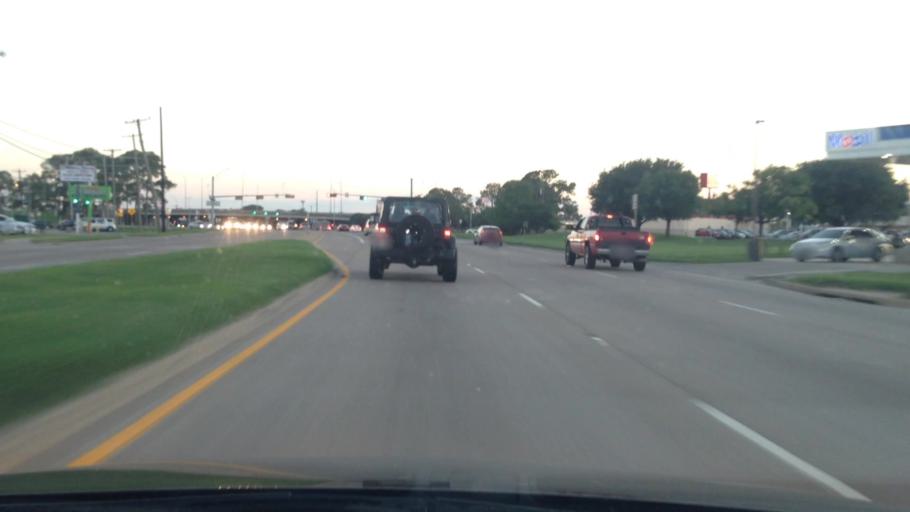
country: US
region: Texas
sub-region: Denton County
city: Lewisville
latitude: 33.0337
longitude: -96.9920
